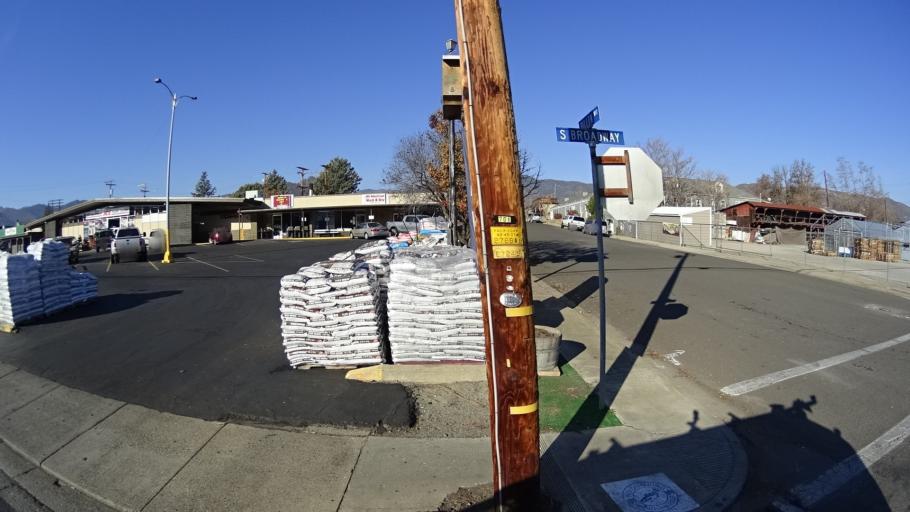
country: US
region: California
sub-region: Siskiyou County
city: Yreka
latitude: 41.7268
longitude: -122.6381
